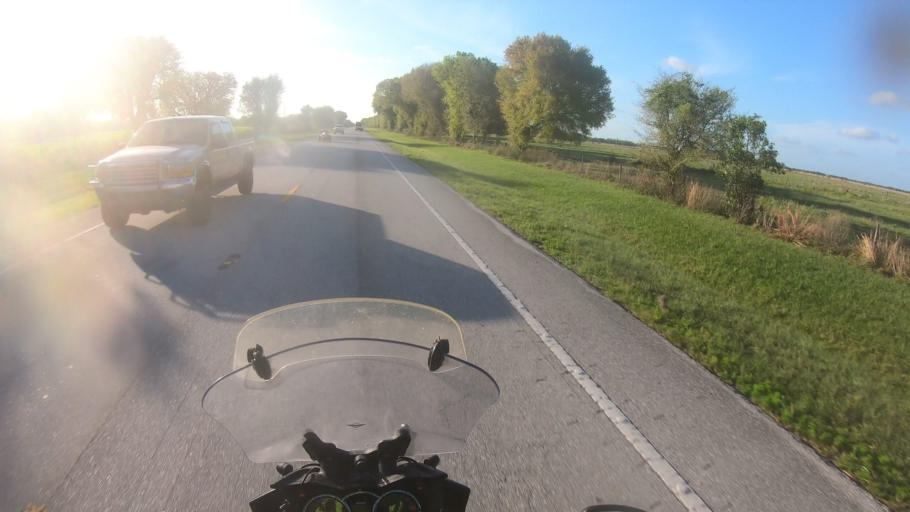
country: US
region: Florida
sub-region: DeSoto County
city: Arcadia
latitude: 27.2762
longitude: -82.0236
